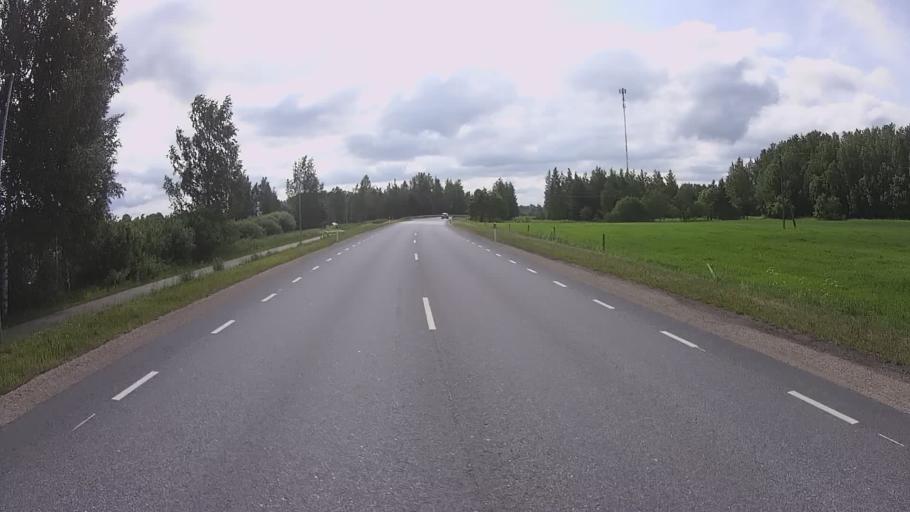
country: EE
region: Polvamaa
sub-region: Polva linn
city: Polva
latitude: 58.1580
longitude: 26.9368
